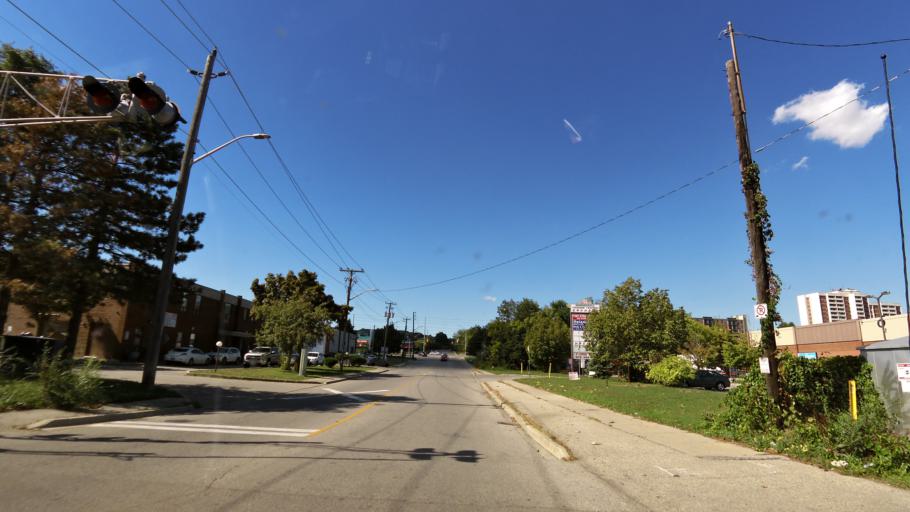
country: CA
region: Ontario
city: Etobicoke
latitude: 43.5964
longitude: -79.5950
